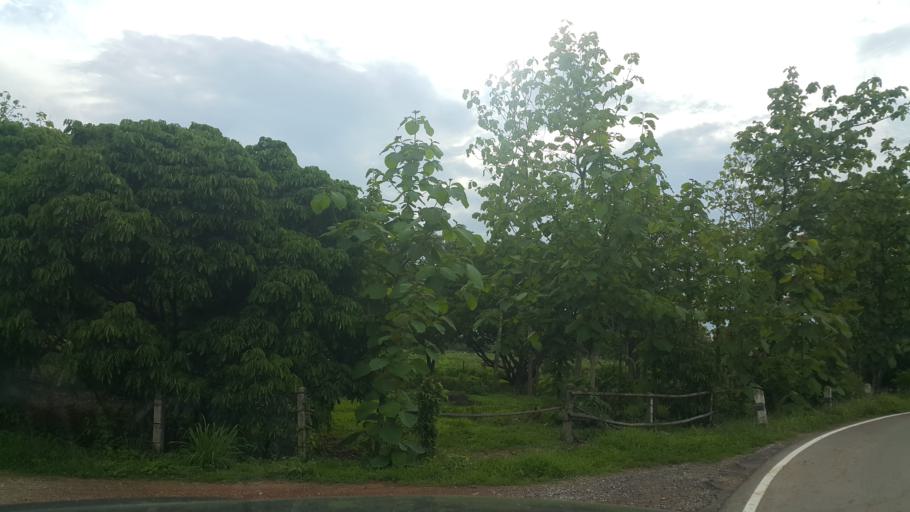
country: TH
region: Chiang Mai
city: Mae On
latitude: 18.7244
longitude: 99.2177
